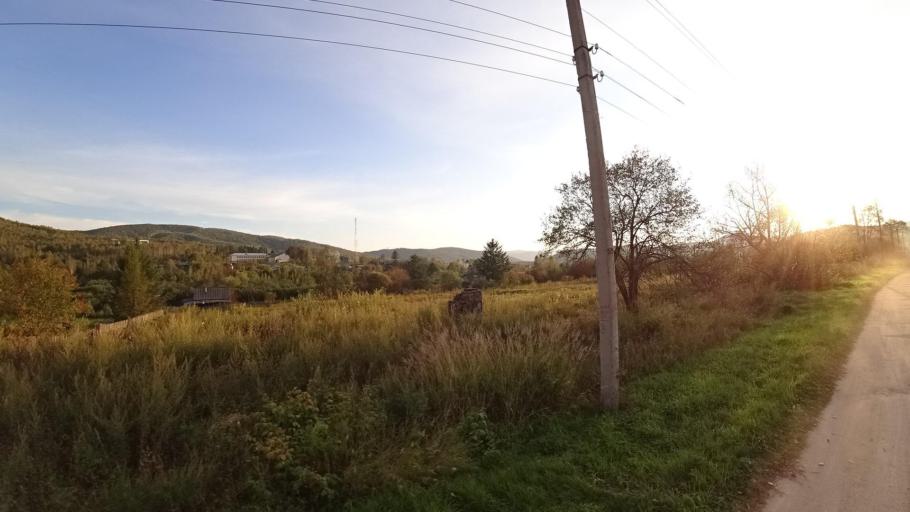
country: RU
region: Jewish Autonomous Oblast
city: Kul'dur
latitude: 49.2078
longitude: 131.6442
